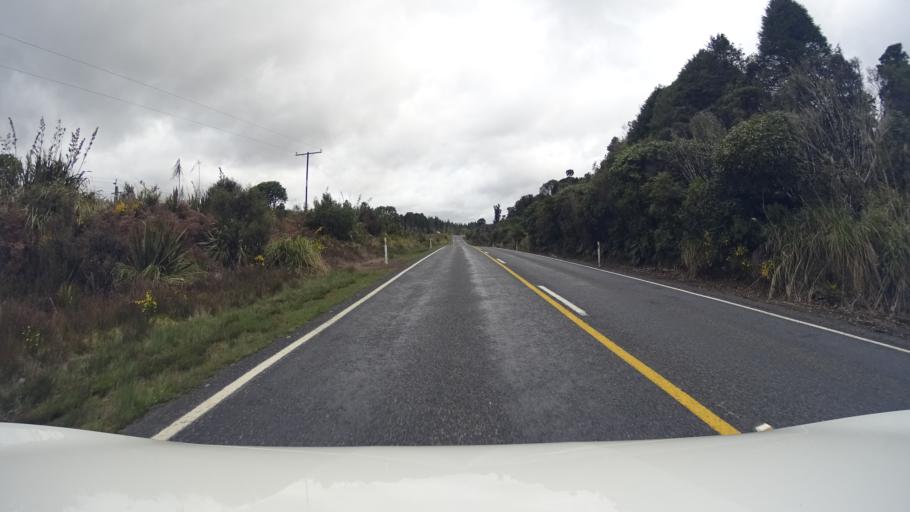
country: NZ
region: Manawatu-Wanganui
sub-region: Ruapehu District
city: Waiouru
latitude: -39.2585
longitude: 175.3886
